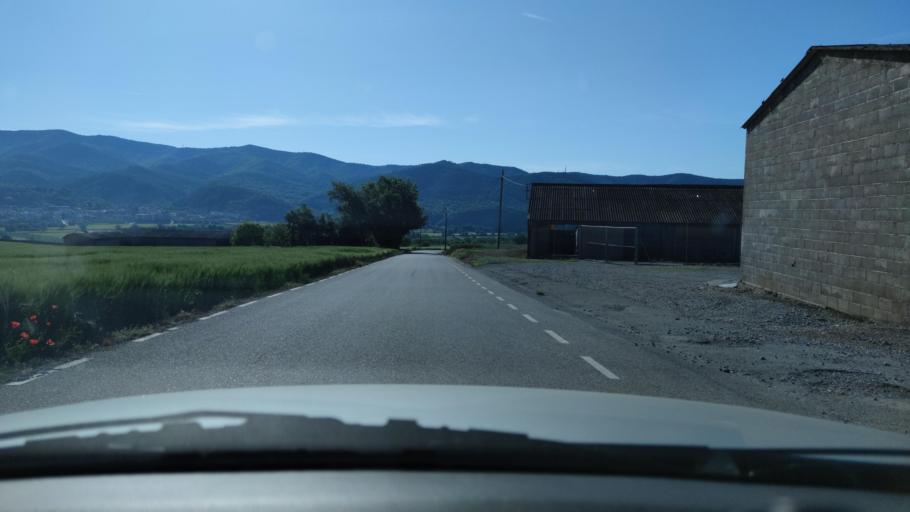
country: ES
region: Catalonia
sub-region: Provincia de Lleida
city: Oliana
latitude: 42.0647
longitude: 1.2901
